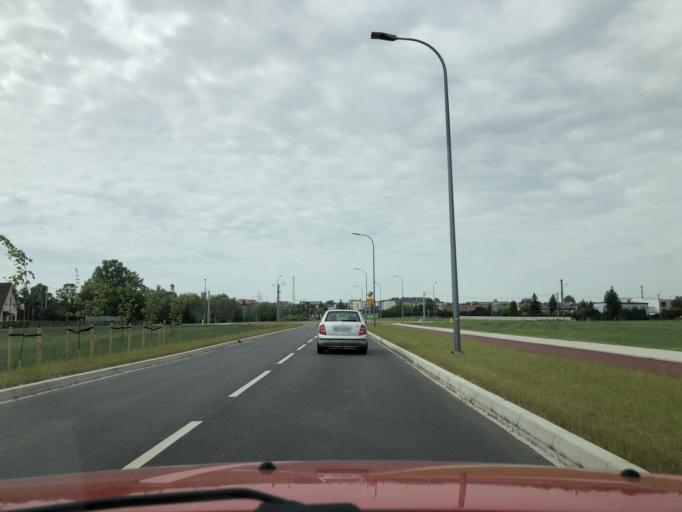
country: PL
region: Greater Poland Voivodeship
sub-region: Powiat jarocinski
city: Jarocin
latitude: 51.9709
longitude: 17.5186
